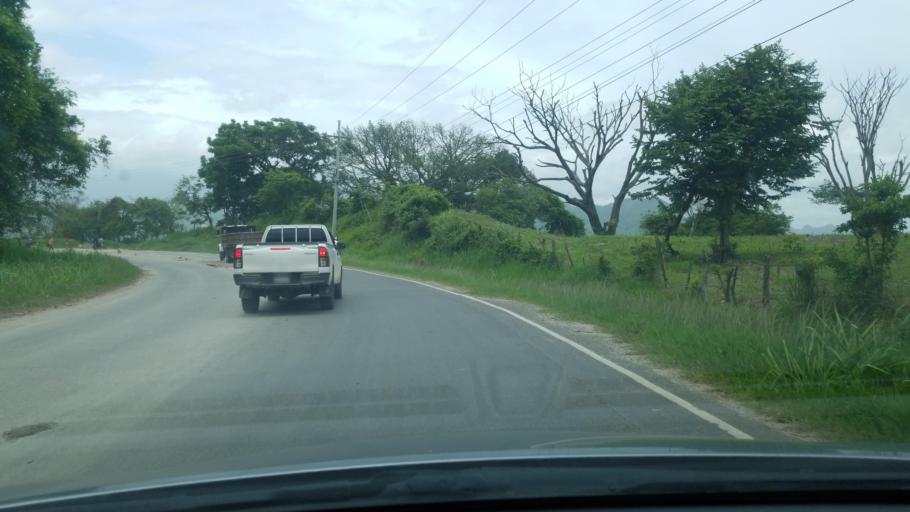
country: HN
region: Copan
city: Santa Rosa de Copan
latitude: 14.7380
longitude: -88.7754
